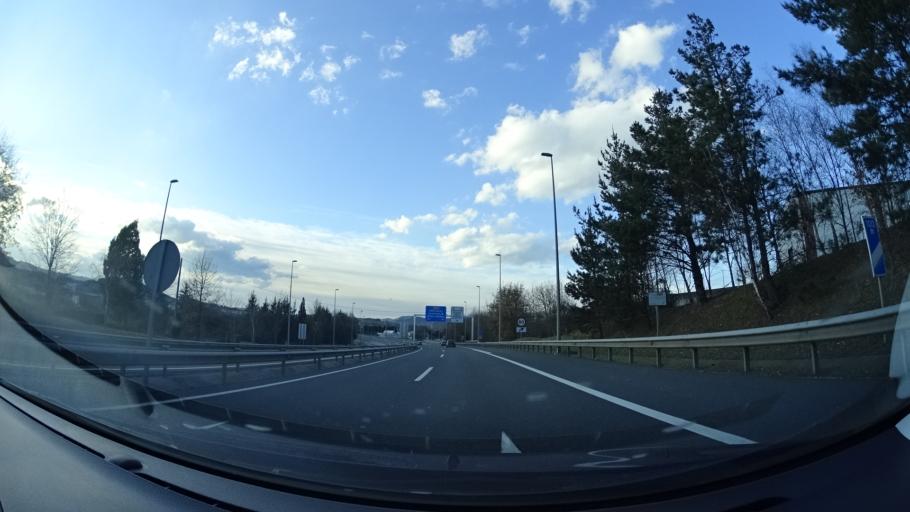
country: ES
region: Basque Country
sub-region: Bizkaia
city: Mungia
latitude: 43.3590
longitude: -2.8412
